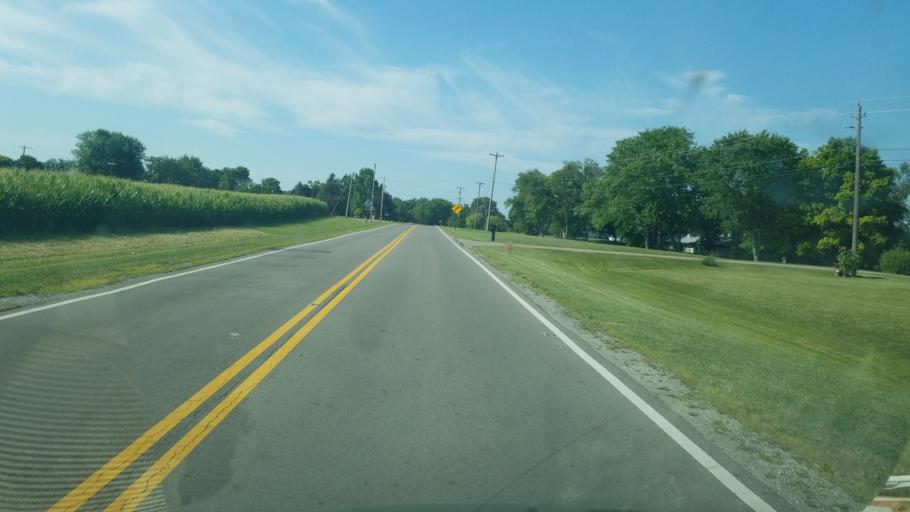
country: US
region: Ohio
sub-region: Franklin County
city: Lincoln Village
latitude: 39.9056
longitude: -83.1457
